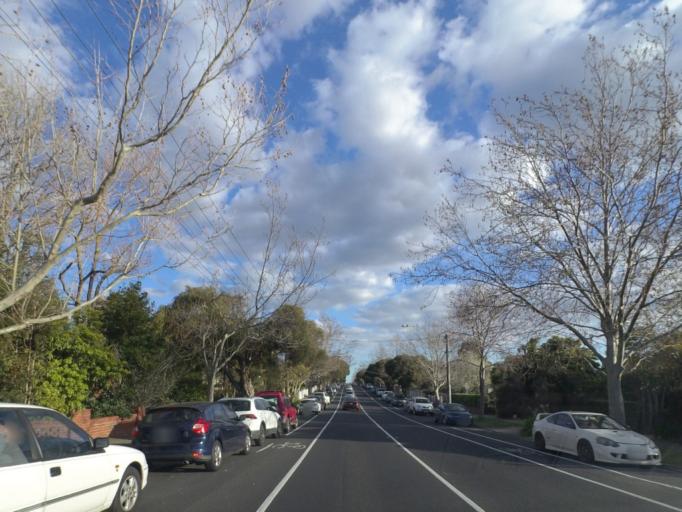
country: AU
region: Victoria
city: Mont Albert
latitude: -37.8163
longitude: 145.0992
